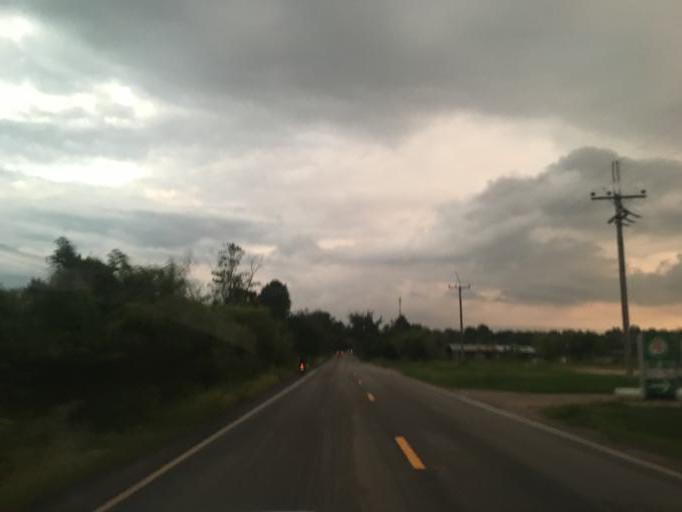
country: TH
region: Changwat Udon Thani
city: Udon Thani
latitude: 17.3234
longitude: 102.7128
